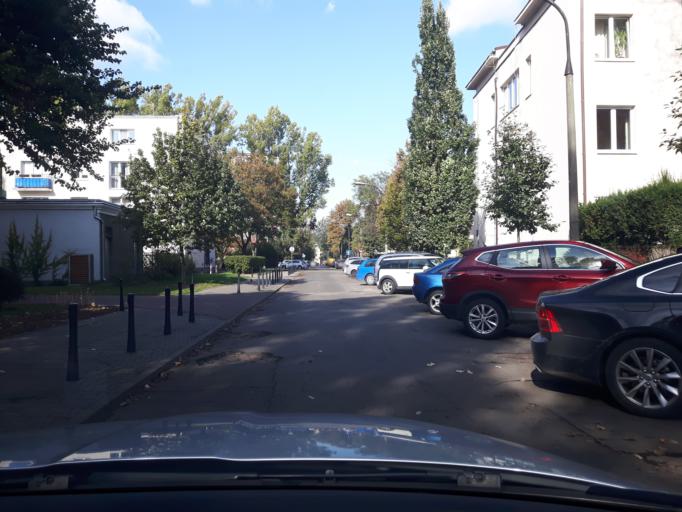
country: PL
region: Masovian Voivodeship
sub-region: Warszawa
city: Praga Poludnie
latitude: 52.2359
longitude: 21.0635
